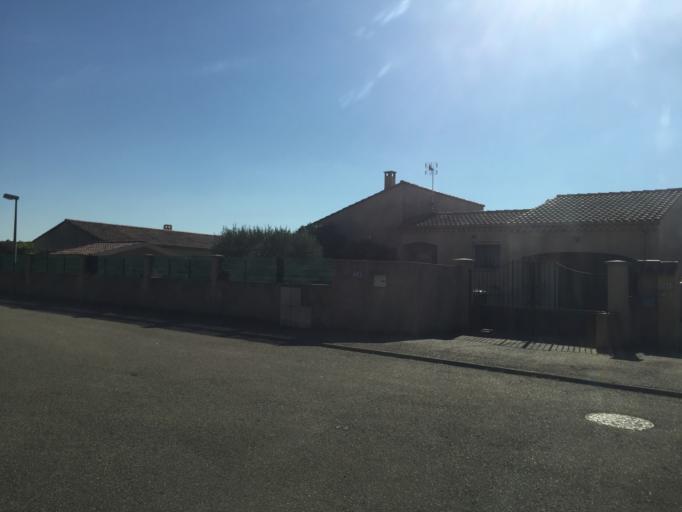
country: FR
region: Provence-Alpes-Cote d'Azur
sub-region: Departement du Vaucluse
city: Sorgues
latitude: 44.0230
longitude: 4.8673
